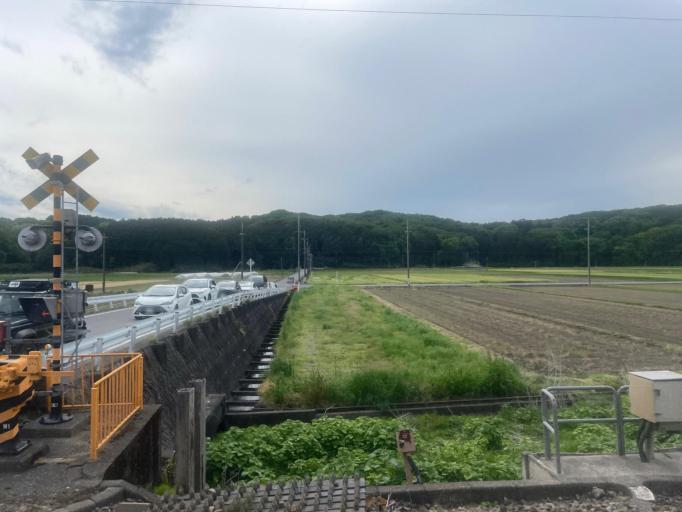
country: JP
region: Tochigi
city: Kanuma
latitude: 36.5050
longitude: 139.7456
